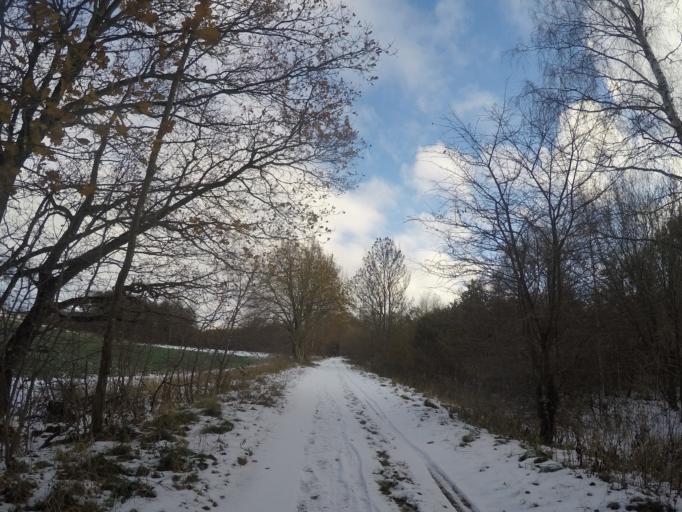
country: SE
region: Skane
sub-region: Lunds Kommun
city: Lund
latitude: 55.7857
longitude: 13.2217
